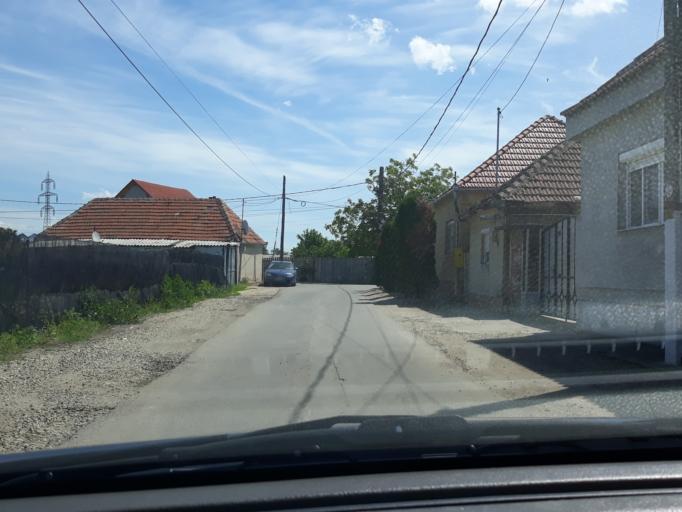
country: RO
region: Bihor
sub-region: Comuna Santandrei
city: Santandrei
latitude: 47.0683
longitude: 21.8572
